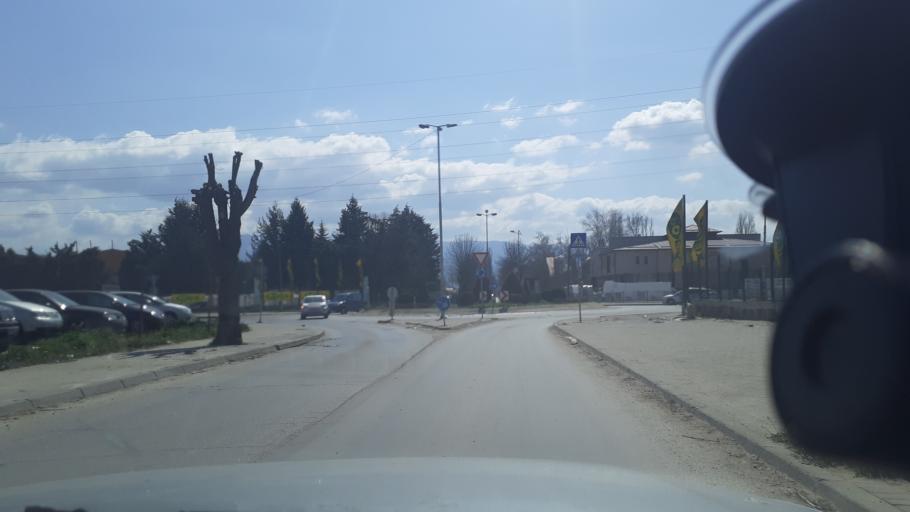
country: MK
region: Tetovo
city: Tetovo
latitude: 41.9998
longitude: 20.9714
